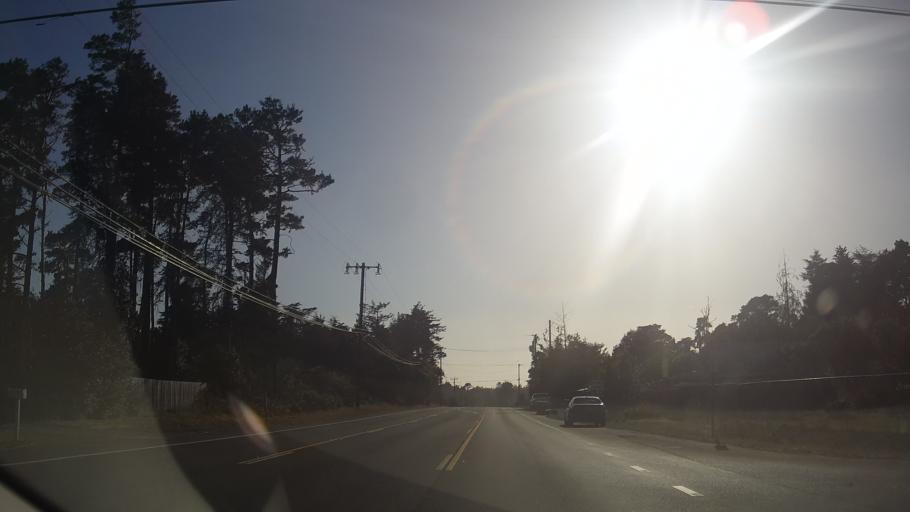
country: US
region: California
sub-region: Mendocino County
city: Fort Bragg
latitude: 39.4155
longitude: -123.7781
